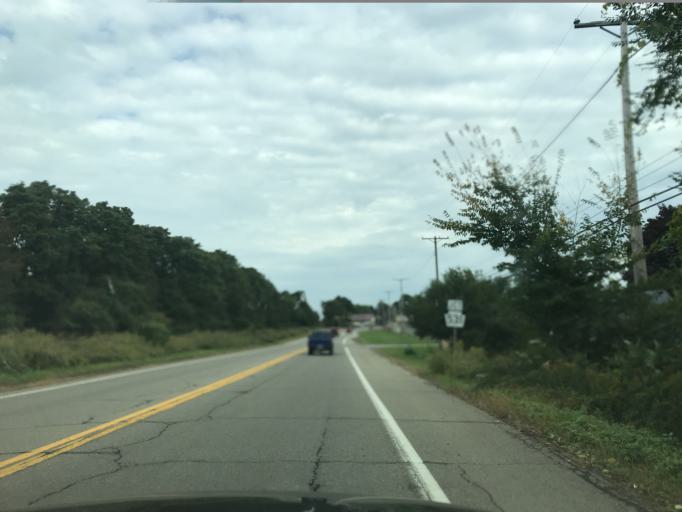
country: US
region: Pennsylvania
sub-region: Erie County
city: Northwest Harborcreek
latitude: 42.1648
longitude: -79.9581
